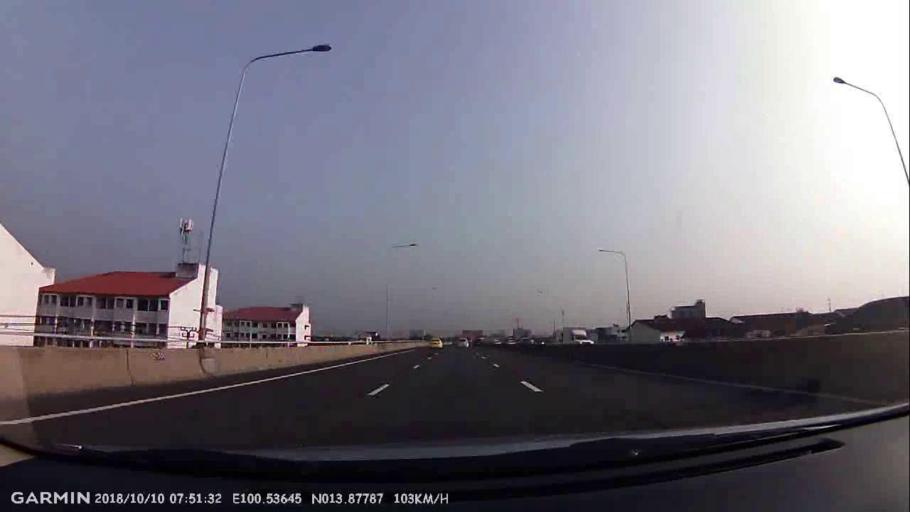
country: TH
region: Nonthaburi
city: Mueang Nonthaburi
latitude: 13.8777
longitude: 100.5357
